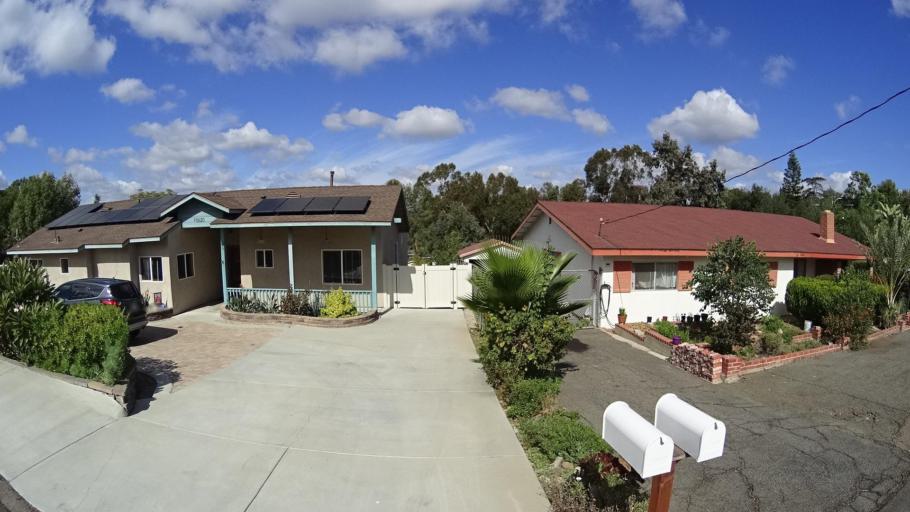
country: US
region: California
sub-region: San Diego County
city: Casa de Oro-Mount Helix
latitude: 32.7396
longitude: -116.9648
